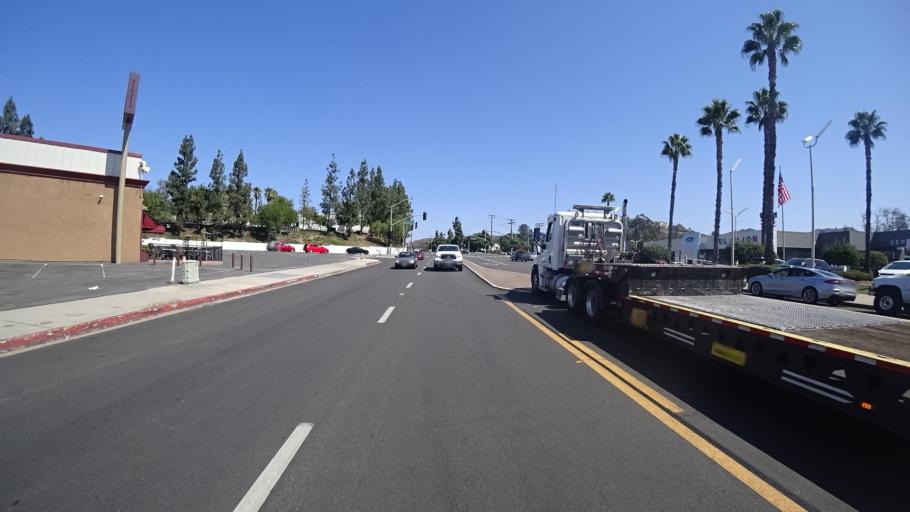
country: US
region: California
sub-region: San Diego County
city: Bostonia
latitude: 32.8072
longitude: -116.9228
